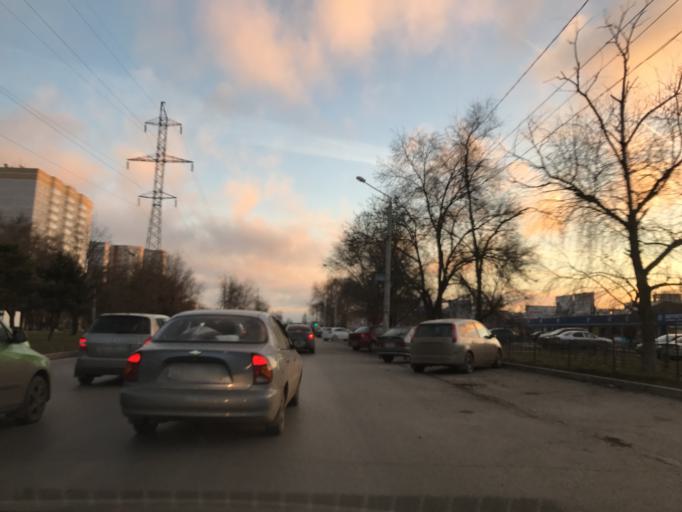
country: RU
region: Rostov
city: Kalinin
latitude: 47.2347
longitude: 39.6135
